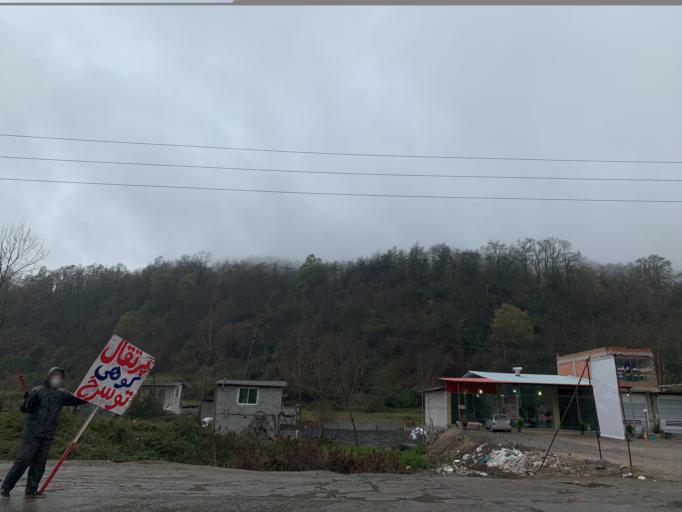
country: IR
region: Mazandaran
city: Amol
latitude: 36.3724
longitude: 52.3535
